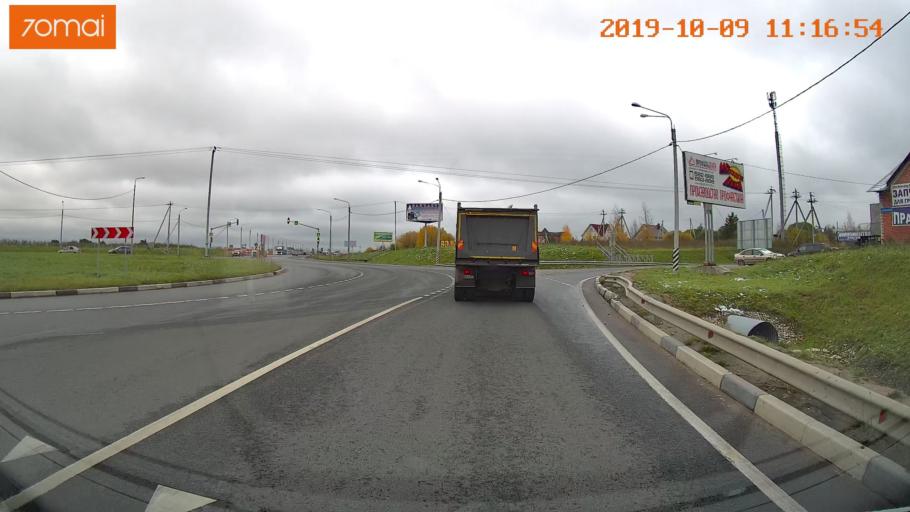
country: RU
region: Vologda
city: Vologda
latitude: 59.1759
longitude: 39.8927
